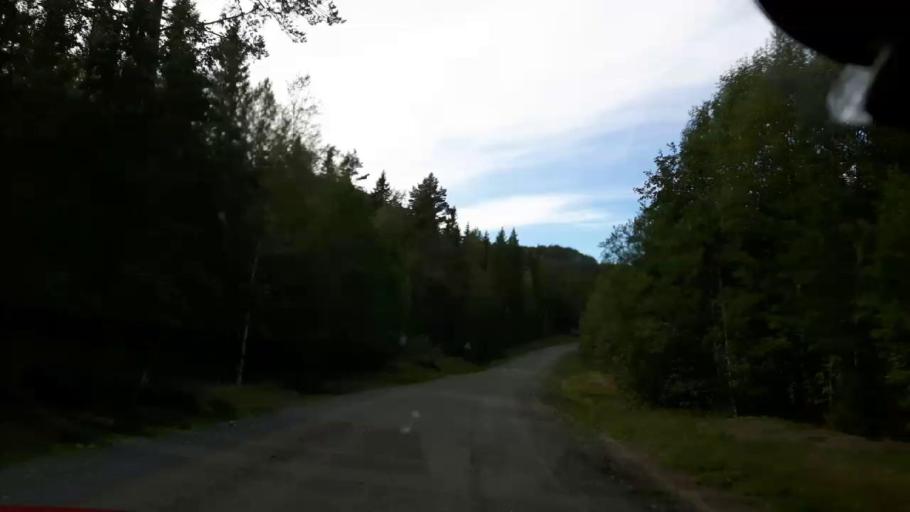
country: SE
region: Jaemtland
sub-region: Ragunda Kommun
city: Hammarstrand
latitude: 63.1159
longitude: 16.0097
